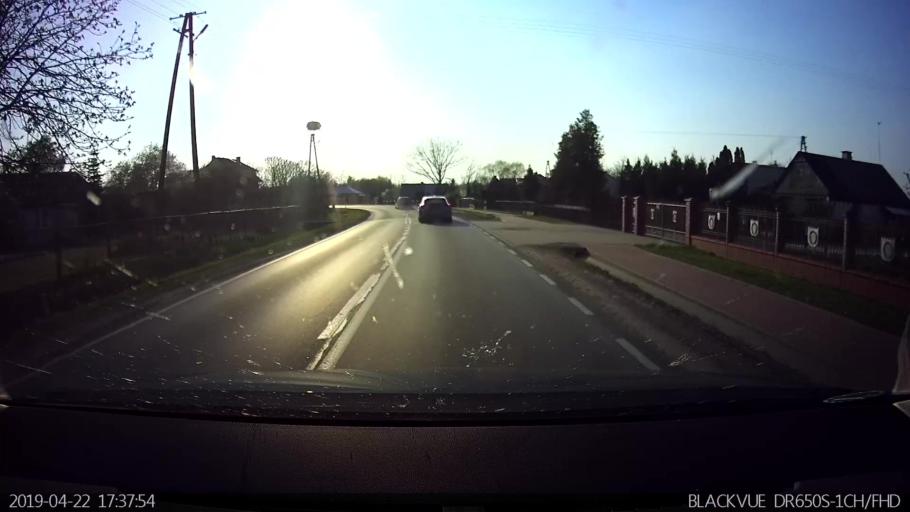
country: PL
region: Masovian Voivodeship
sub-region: Powiat sokolowski
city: Sokolow Podlaski
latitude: 52.4106
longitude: 22.1680
